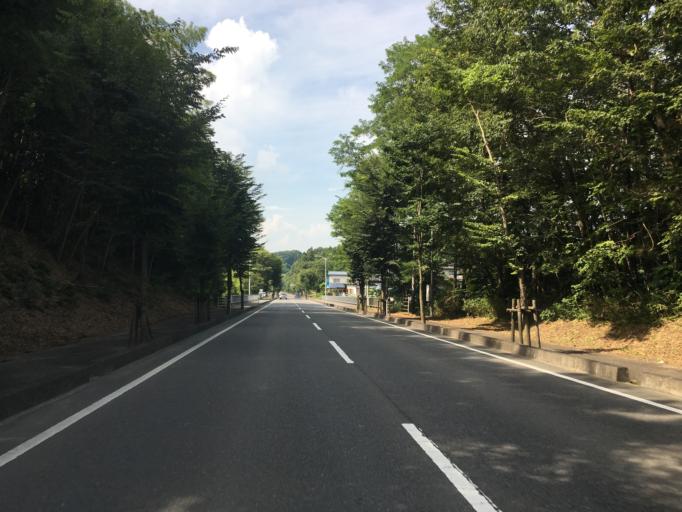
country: JP
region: Fukushima
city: Sukagawa
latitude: 37.2377
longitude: 140.4355
